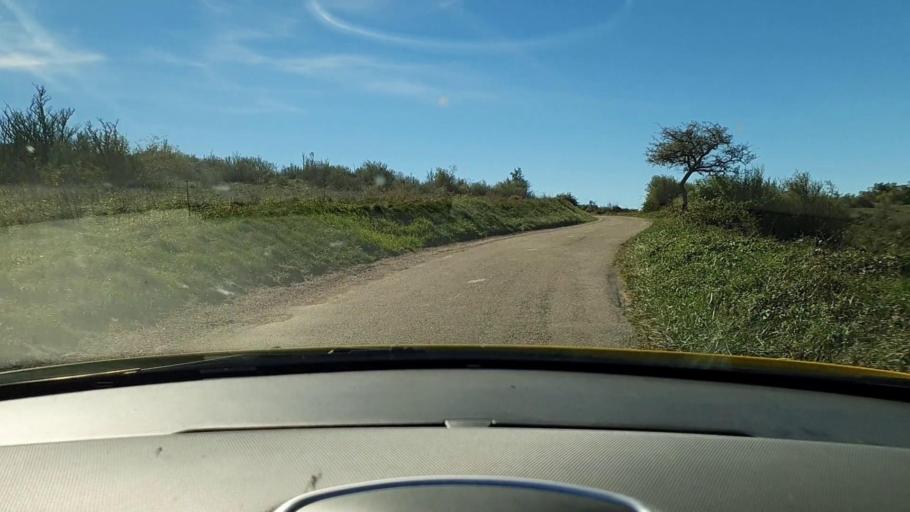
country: FR
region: Languedoc-Roussillon
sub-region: Departement du Gard
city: Aveze
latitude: 43.9602
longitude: 3.4252
